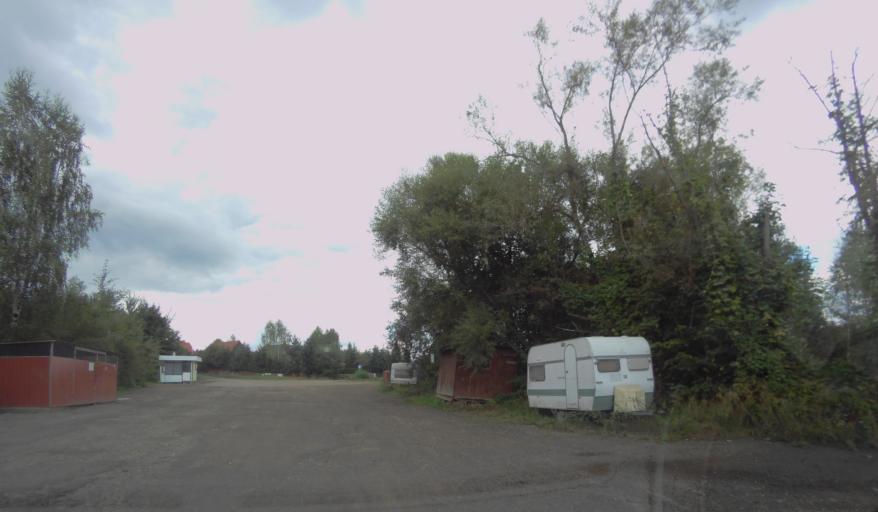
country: PL
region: Subcarpathian Voivodeship
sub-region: Powiat leski
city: Polanczyk
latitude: 49.3135
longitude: 22.5076
